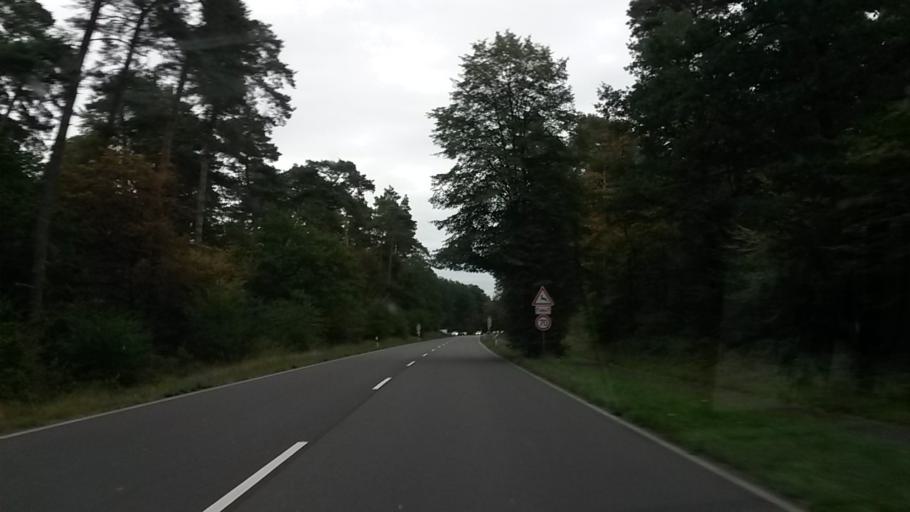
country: DE
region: North Rhine-Westphalia
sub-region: Regierungsbezirk Koln
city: Rath
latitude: 50.9396
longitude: 7.1105
